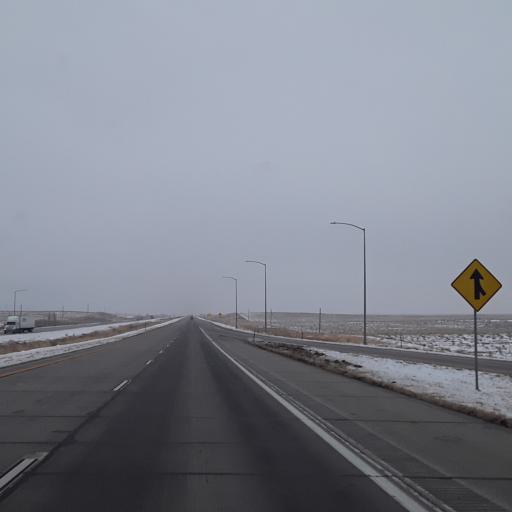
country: US
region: Colorado
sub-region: Logan County
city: Sterling
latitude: 40.5025
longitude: -103.2586
